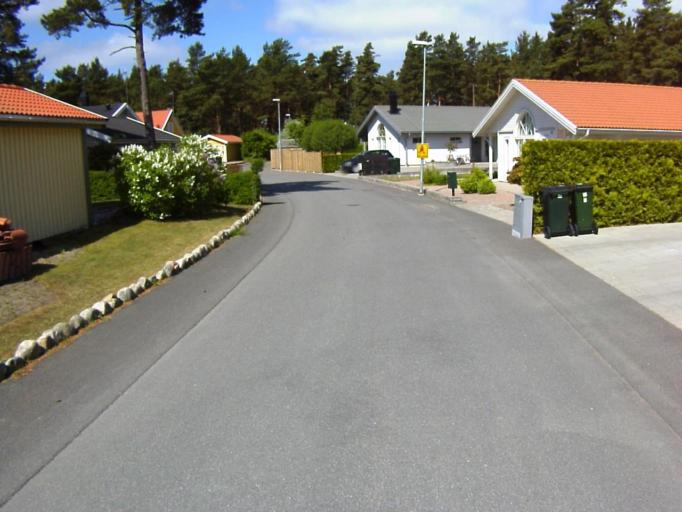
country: SE
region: Skane
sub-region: Kristianstads Kommun
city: Ahus
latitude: 55.9410
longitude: 14.3040
